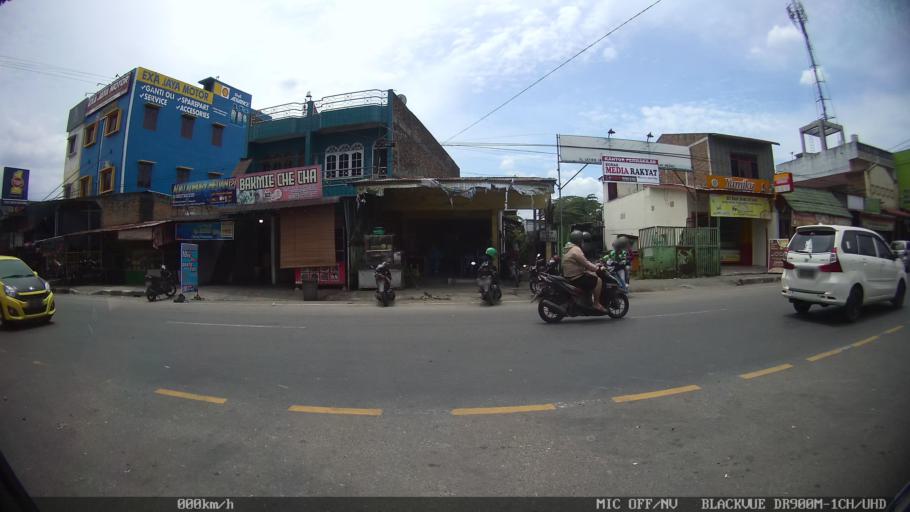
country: ID
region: North Sumatra
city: Deli Tua
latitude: 3.5358
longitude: 98.6500
